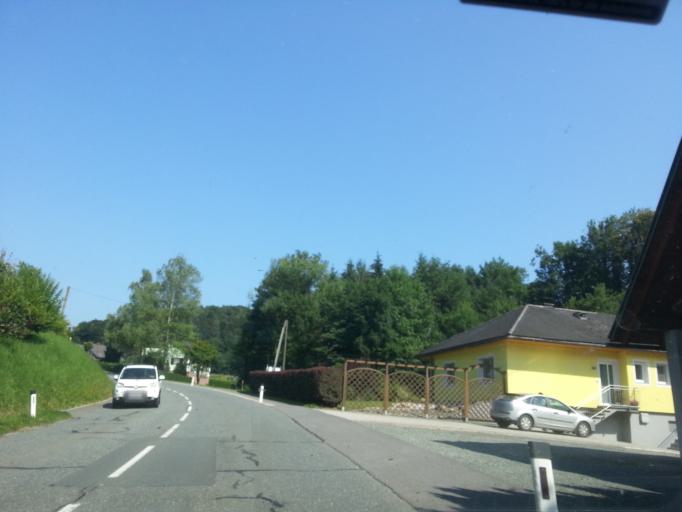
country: AT
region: Styria
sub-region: Politischer Bezirk Leibnitz
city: Grossklein
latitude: 46.7342
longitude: 15.4503
